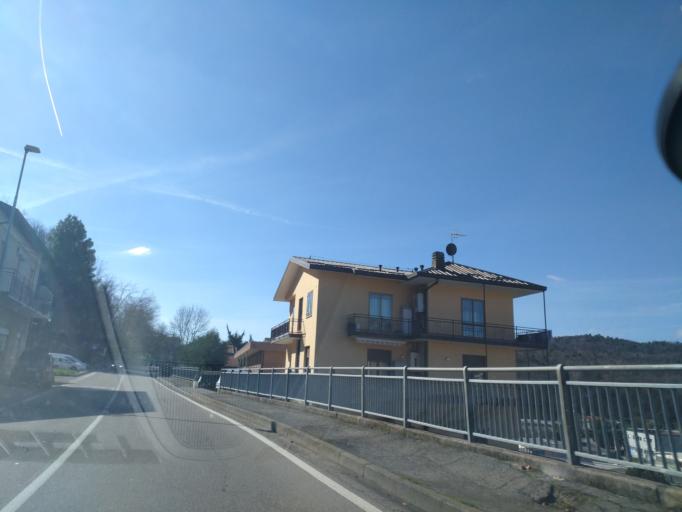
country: IT
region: Lombardy
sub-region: Provincia di Como
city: Lipomo
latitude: 45.7928
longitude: 9.1263
